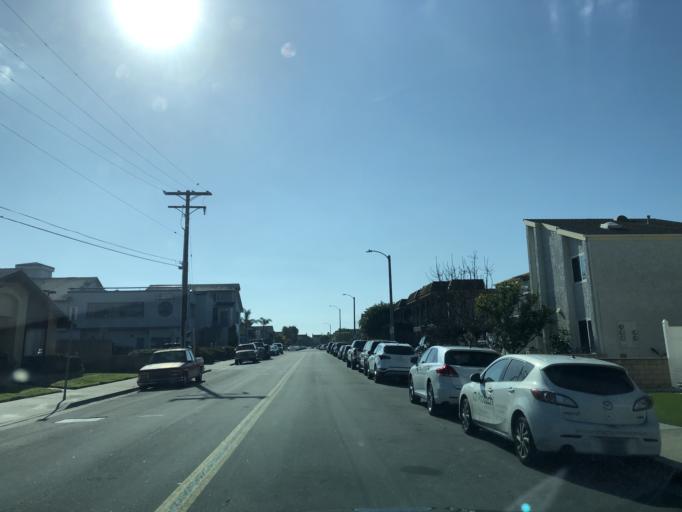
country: US
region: California
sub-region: Orange County
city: Westminster
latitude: 33.7166
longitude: -118.0436
